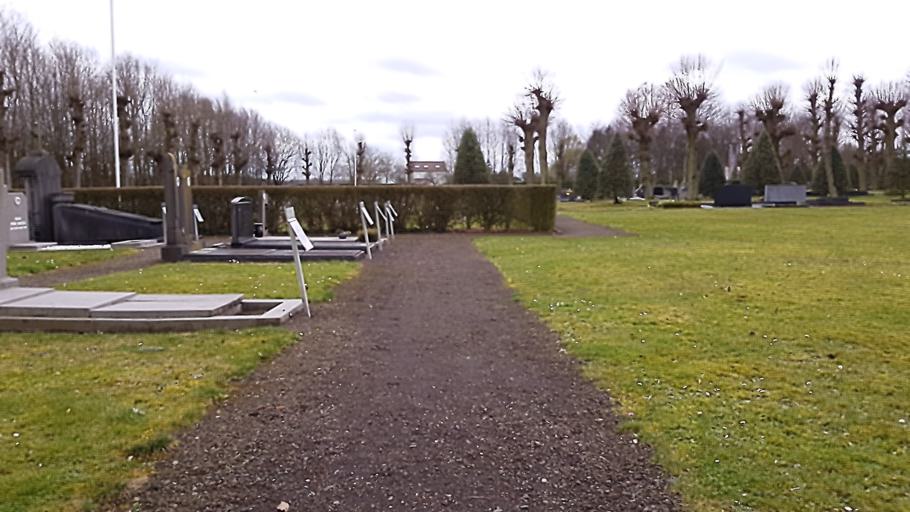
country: BE
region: Flanders
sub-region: Provincie Antwerpen
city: Boechout
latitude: 51.1561
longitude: 4.4858
